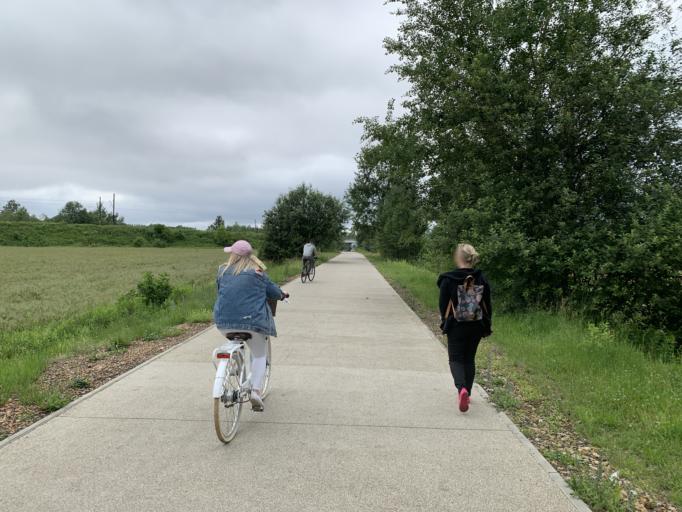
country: PL
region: Silesian Voivodeship
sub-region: Bytom
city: Bytom
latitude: 50.3326
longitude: 18.9515
